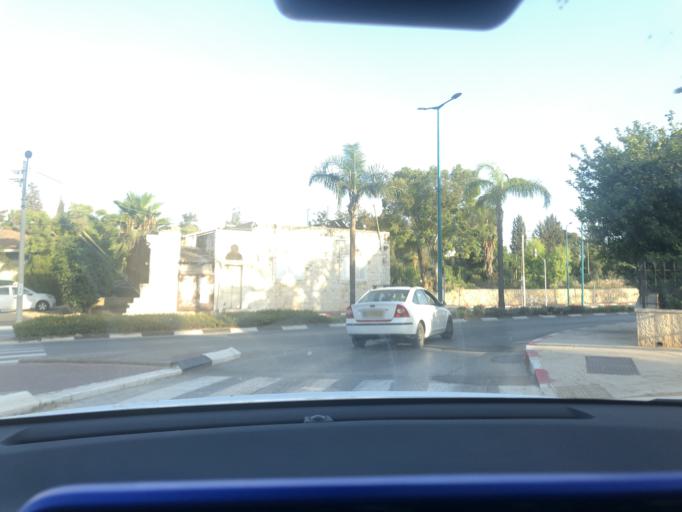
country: IL
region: Central District
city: Lod
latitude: 31.9505
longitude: 34.8955
